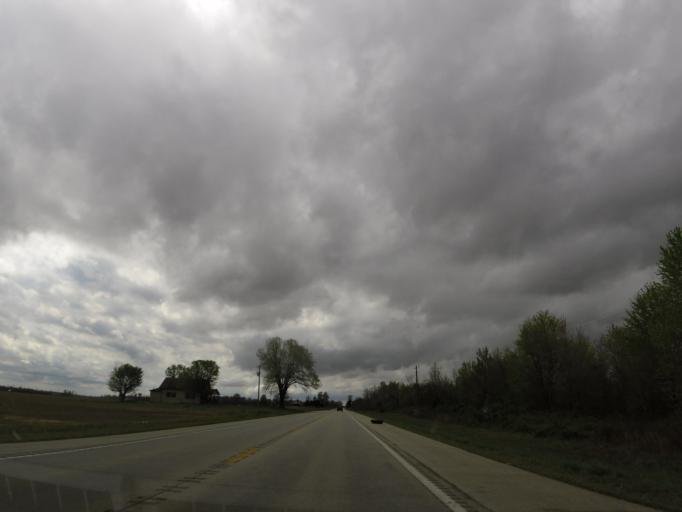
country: US
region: Missouri
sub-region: Butler County
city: Poplar Bluff
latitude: 36.6043
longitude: -90.5205
